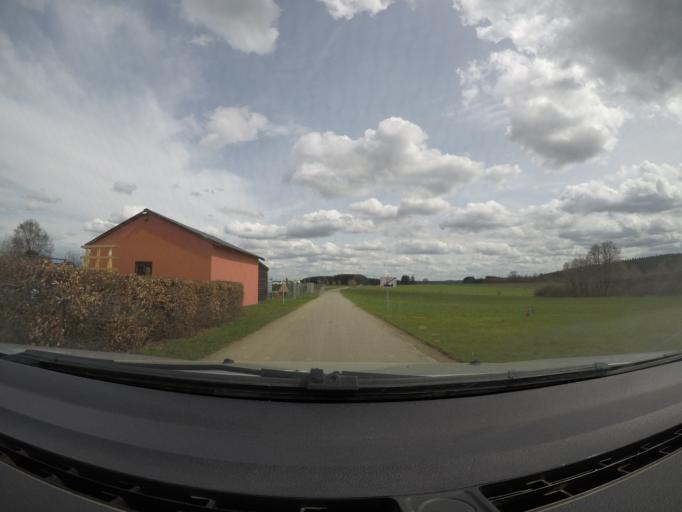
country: BE
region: Wallonia
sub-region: Province du Luxembourg
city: Leglise
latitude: 49.7970
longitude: 5.4818
